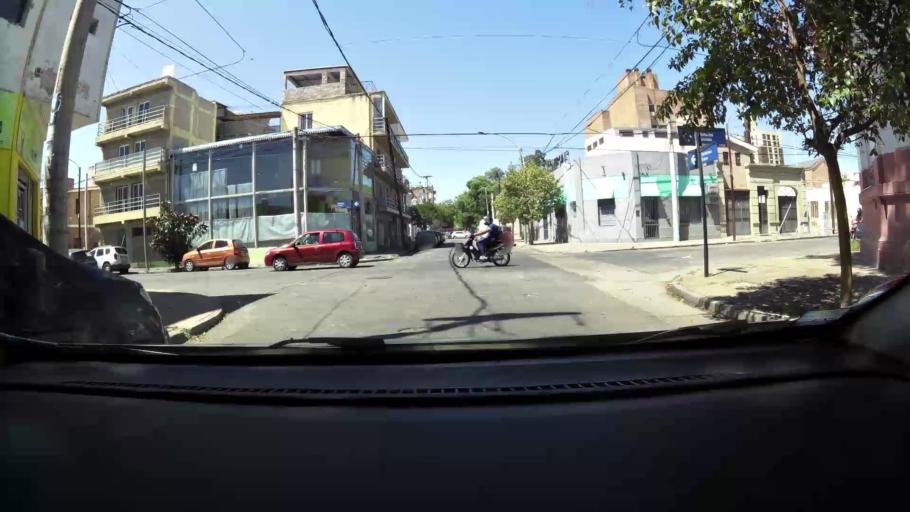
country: AR
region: Cordoba
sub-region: Departamento de Capital
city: Cordoba
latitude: -31.4222
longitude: -64.1478
